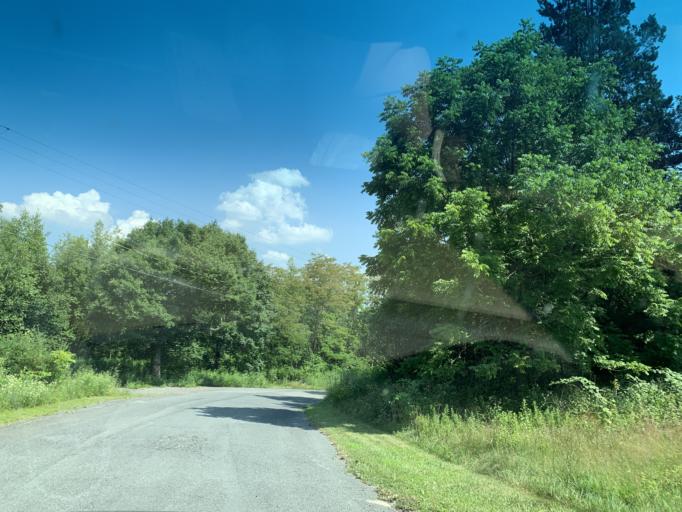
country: US
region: Pennsylvania
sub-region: Schuylkill County
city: Ashland
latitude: 40.8081
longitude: -76.3431
